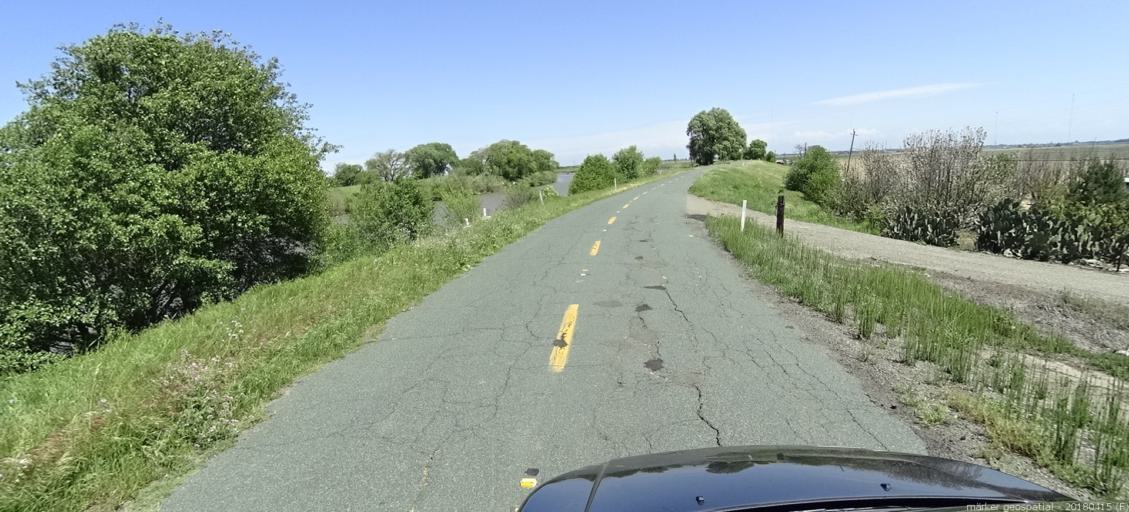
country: US
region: California
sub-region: Sacramento County
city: Walnut Grove
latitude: 38.2534
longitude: -121.6003
